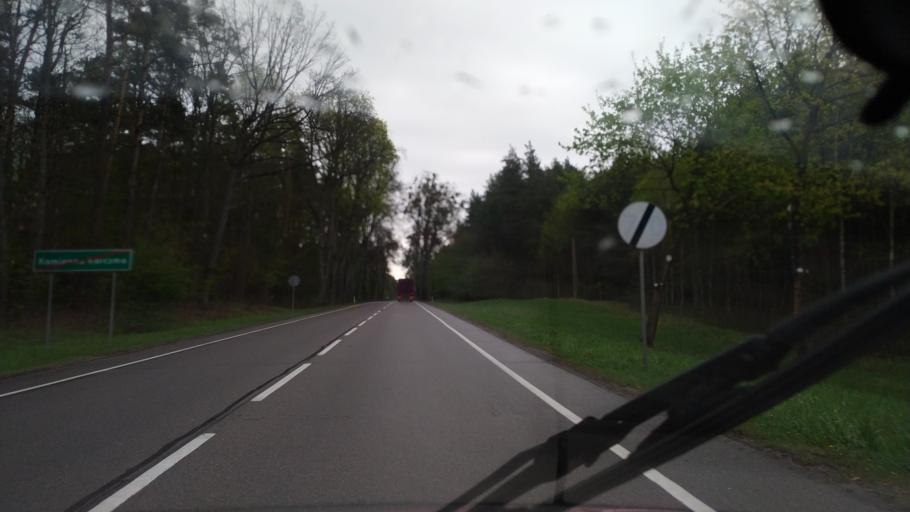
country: PL
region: Pomeranian Voivodeship
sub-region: Powiat starogardzki
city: Kaliska
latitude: 53.8786
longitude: 18.1836
